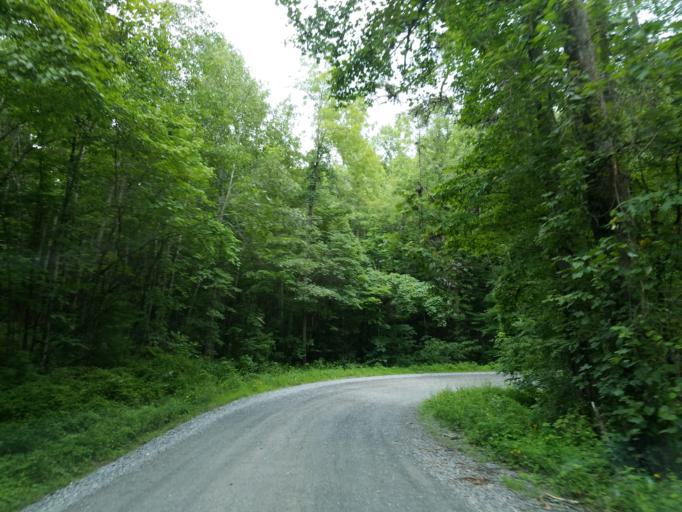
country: US
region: Georgia
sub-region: Fannin County
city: Blue Ridge
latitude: 34.8267
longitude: -84.2300
